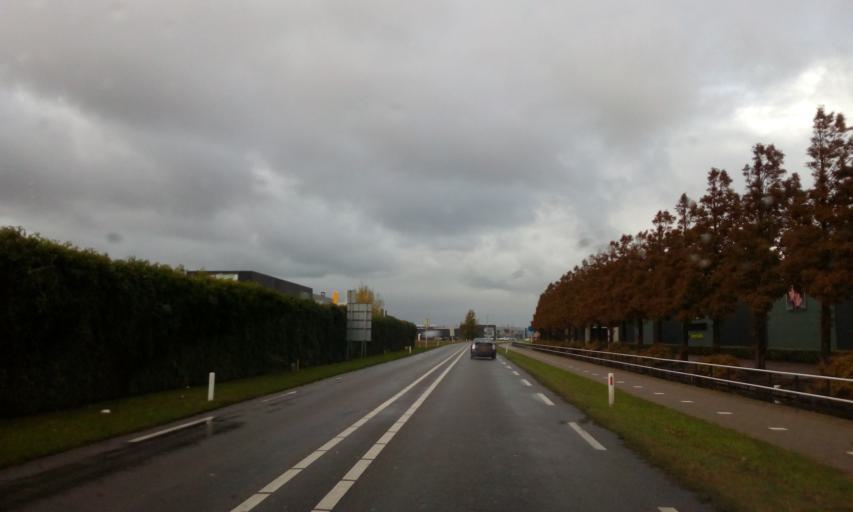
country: NL
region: South Holland
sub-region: Gemeente Westland
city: Honselersdijk
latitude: 52.0021
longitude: 4.2170
